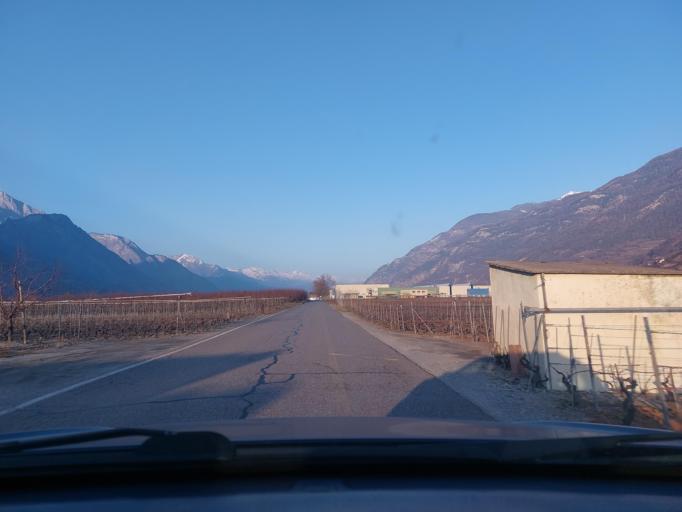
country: CH
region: Valais
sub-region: Martigny District
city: Saxon
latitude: 46.1456
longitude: 7.1598
